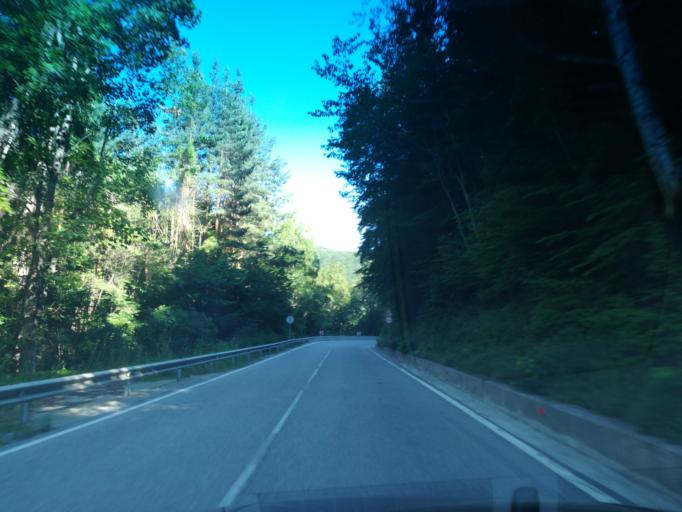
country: BG
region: Smolyan
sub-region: Obshtina Chepelare
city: Chepelare
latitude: 41.8123
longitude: 24.7044
